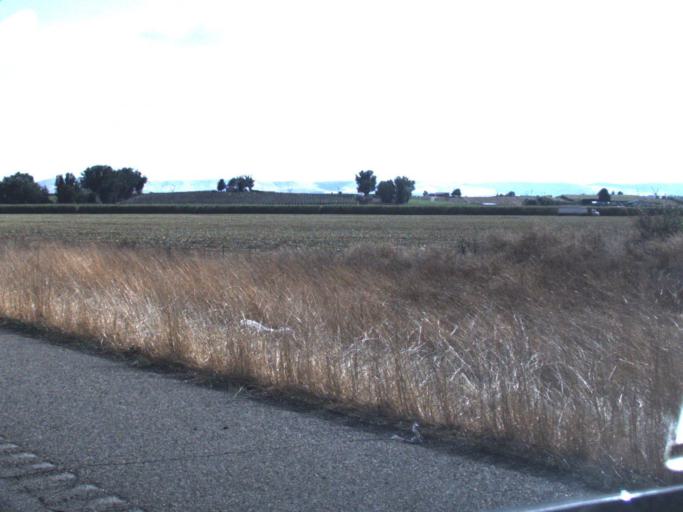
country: US
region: Washington
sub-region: Yakima County
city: Sunnyside
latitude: 46.3014
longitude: -119.9655
